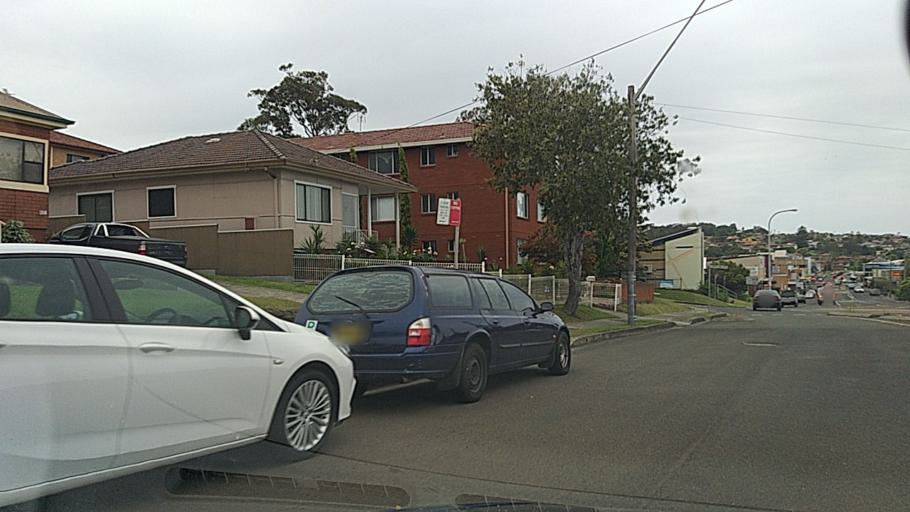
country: AU
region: New South Wales
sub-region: Wollongong
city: Lake Heights
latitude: -34.4857
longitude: 150.8839
